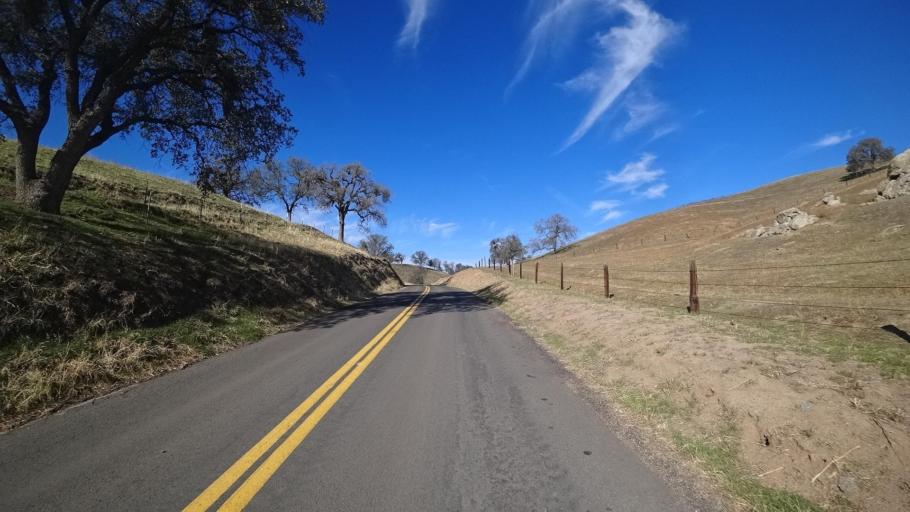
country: US
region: California
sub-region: Kern County
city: Oildale
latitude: 35.6589
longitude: -118.8429
